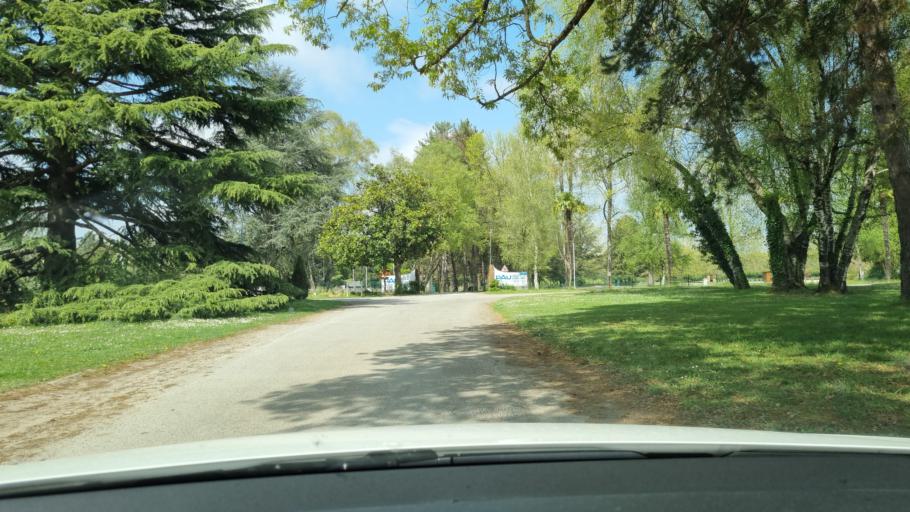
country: FR
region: Aquitaine
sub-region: Departement des Pyrenees-Atlantiques
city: Montardon
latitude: 43.3487
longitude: -0.3760
